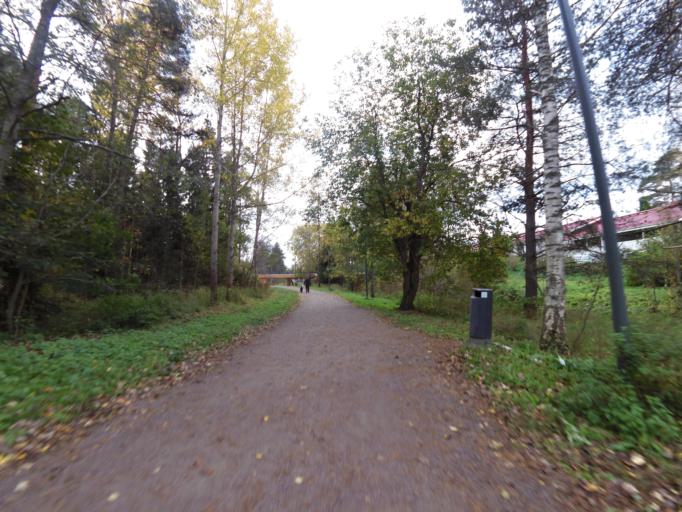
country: FI
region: Uusimaa
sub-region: Helsinki
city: Espoo
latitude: 60.1959
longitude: 24.6757
